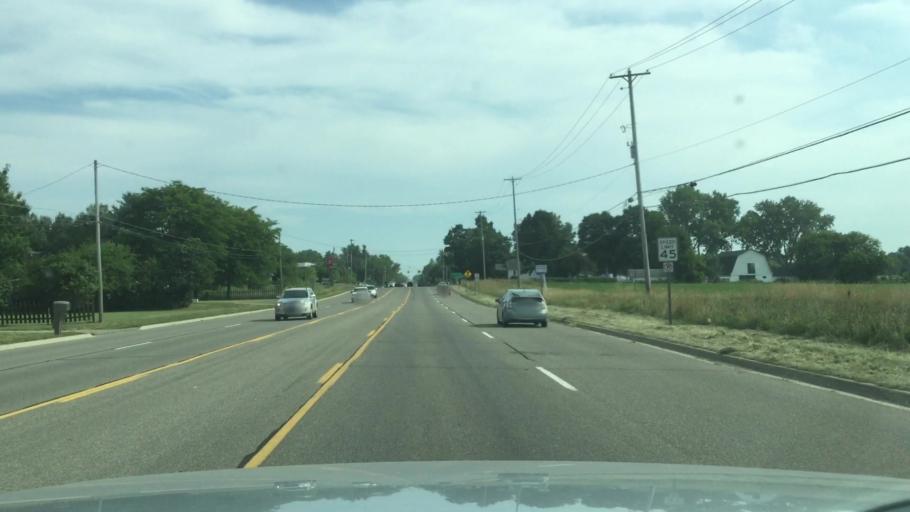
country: US
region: Michigan
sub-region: Genesee County
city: Swartz Creek
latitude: 43.0042
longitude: -83.8122
